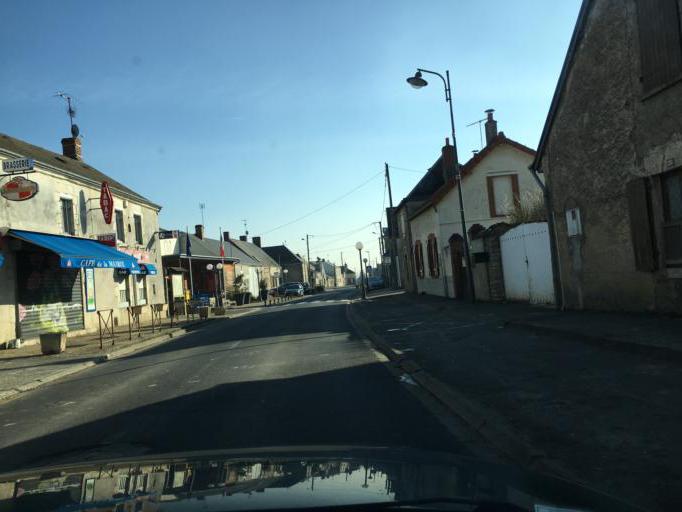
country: FR
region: Centre
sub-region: Departement du Loiret
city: Bricy
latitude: 48.0538
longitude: 1.7900
